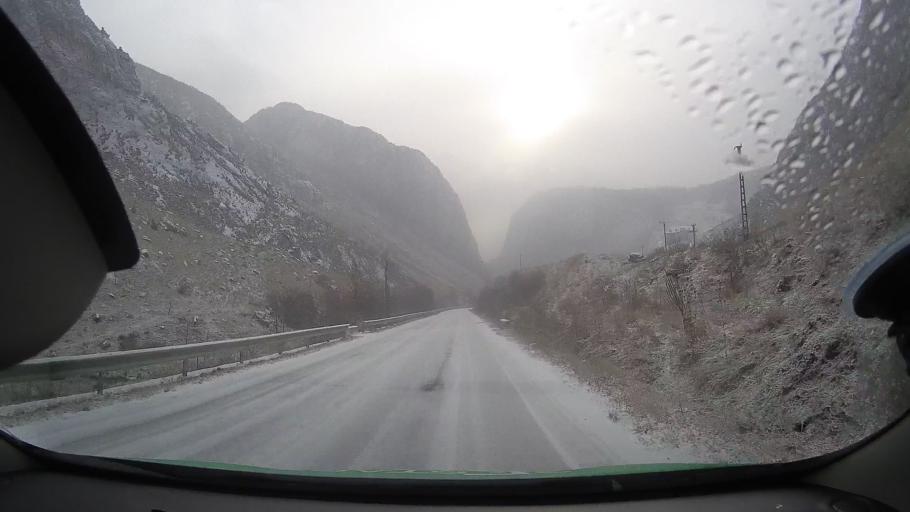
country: RO
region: Alba
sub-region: Comuna Livezile
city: Livezile
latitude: 46.3805
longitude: 23.5820
